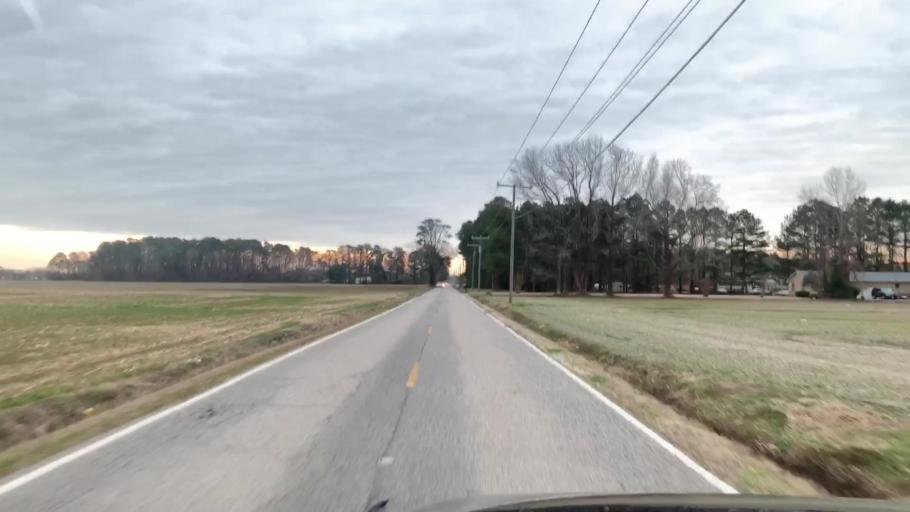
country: US
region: North Carolina
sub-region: Currituck County
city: Moyock
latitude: 36.6327
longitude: -76.1823
